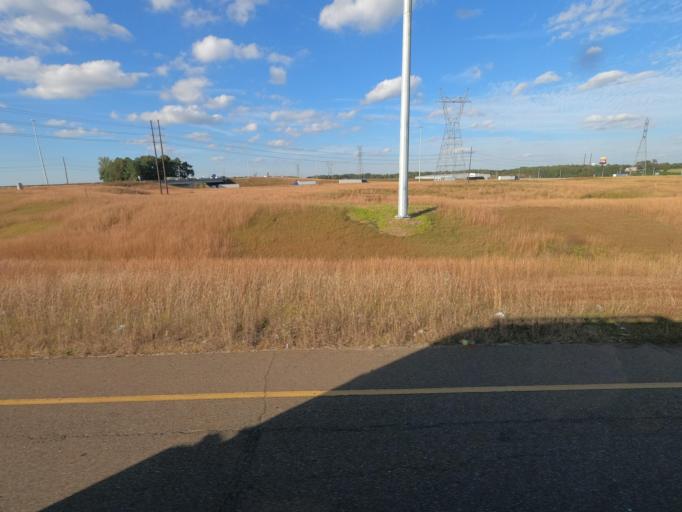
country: US
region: Tennessee
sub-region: Madison County
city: Jackson
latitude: 35.6772
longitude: -88.7797
